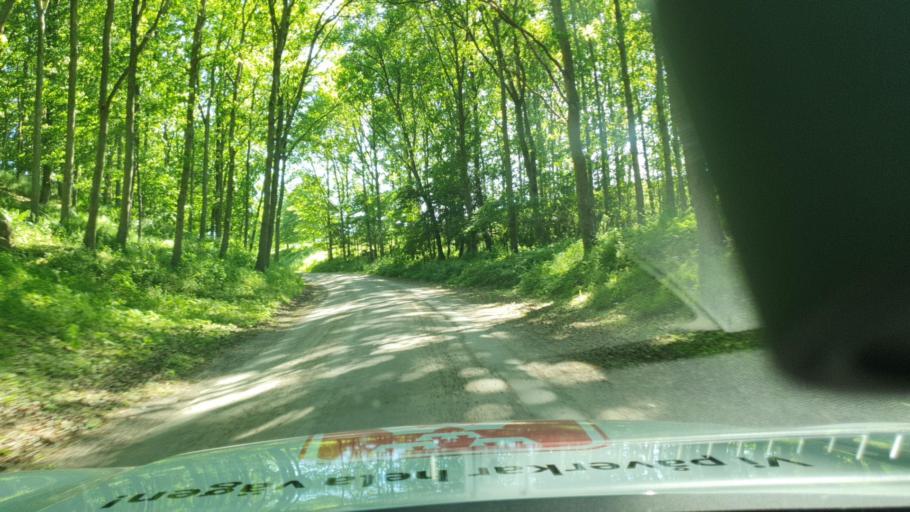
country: SE
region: Skane
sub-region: Ystads Kommun
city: Kopingebro
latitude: 55.5128
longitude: 13.8920
